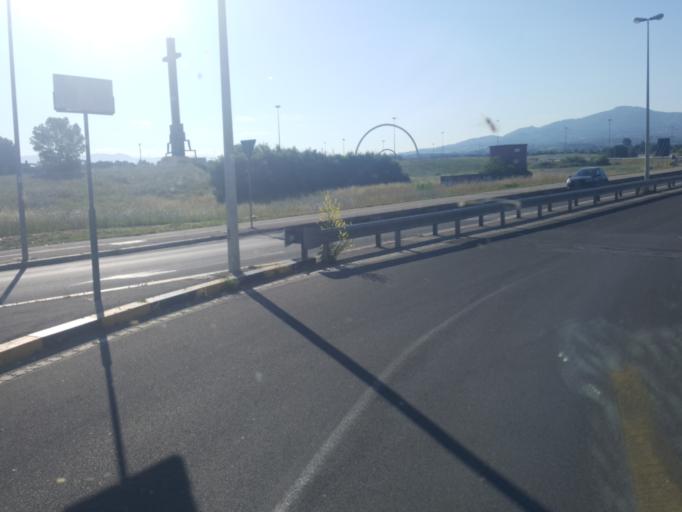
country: IT
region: Latium
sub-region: Citta metropolitana di Roma Capitale
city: Frascati
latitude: 41.8529
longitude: 12.6332
